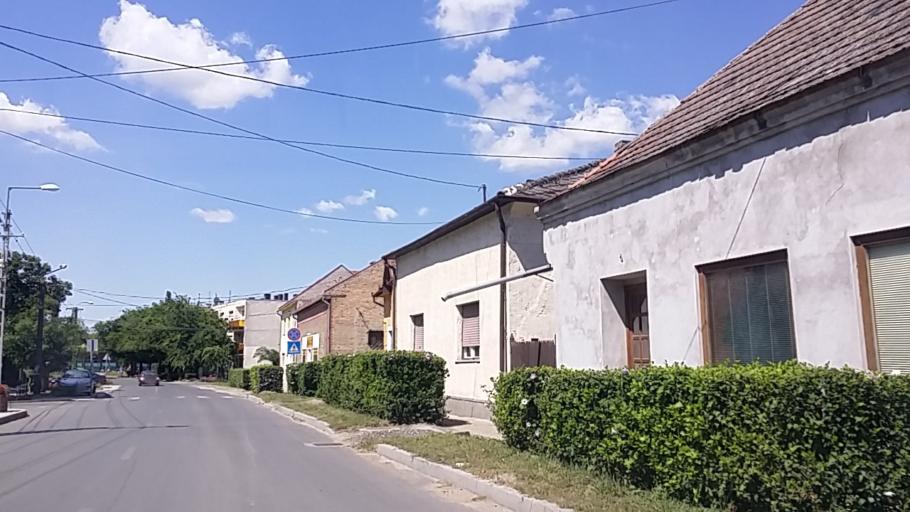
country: HU
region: Tolna
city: Simontornya
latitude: 46.7538
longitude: 18.5526
